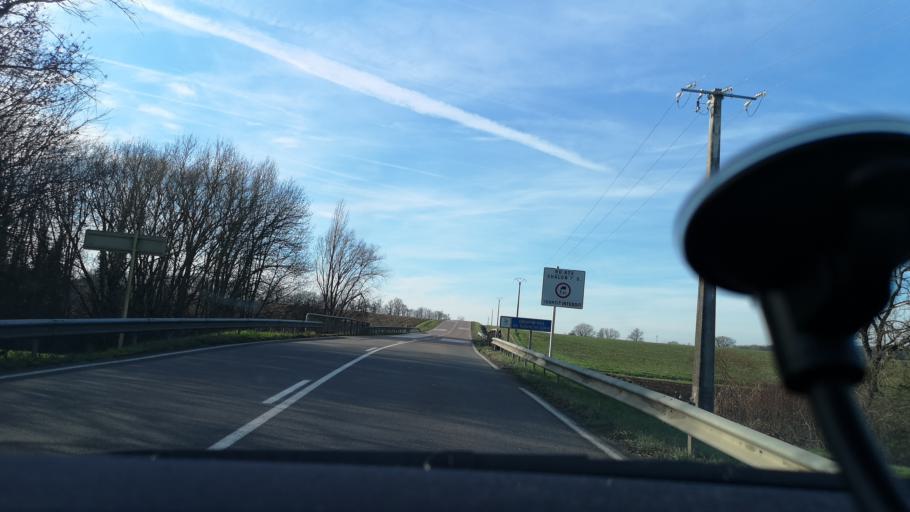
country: FR
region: Franche-Comte
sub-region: Departement du Jura
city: Petit-Noir
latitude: 46.9612
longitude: 5.2635
